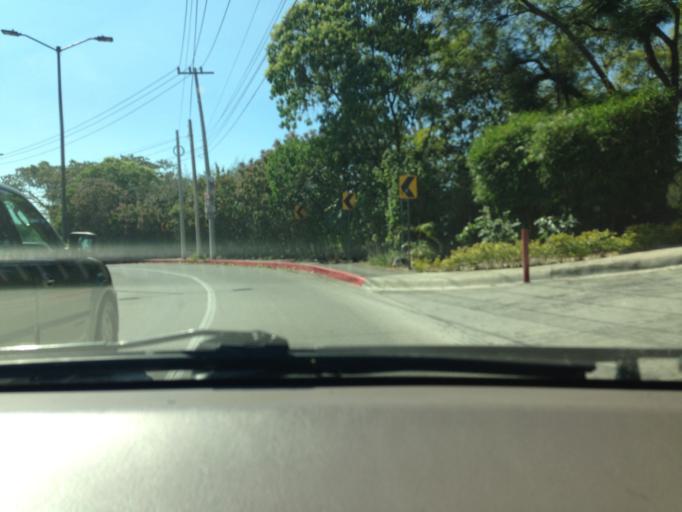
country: MX
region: Morelos
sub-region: Cuernavaca
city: Fraccionamiento Lomas de Ahuatlan
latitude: 18.9571
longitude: -99.2395
